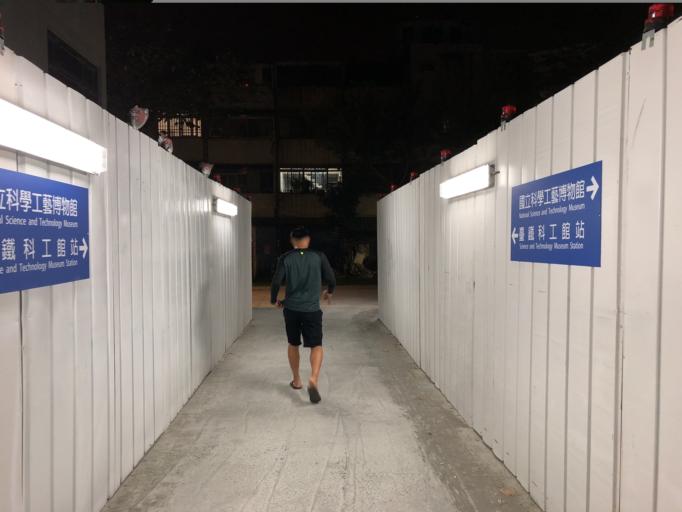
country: TW
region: Kaohsiung
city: Kaohsiung
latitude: 22.6373
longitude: 120.3258
